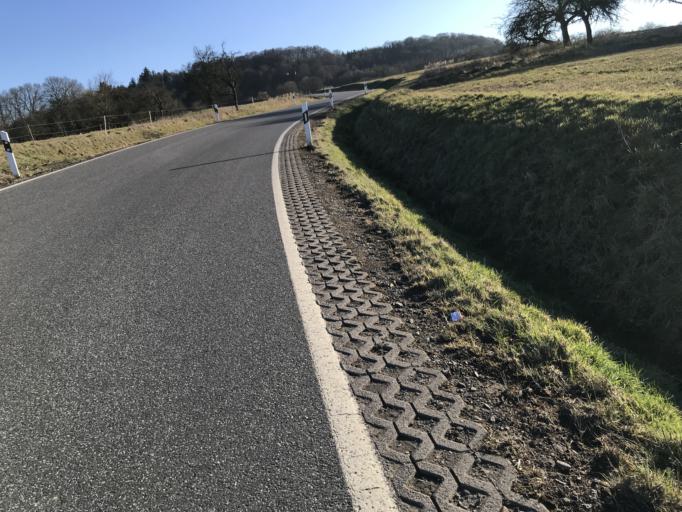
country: DE
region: Hesse
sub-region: Regierungsbezirk Giessen
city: Rabenau
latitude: 50.6717
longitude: 8.8566
